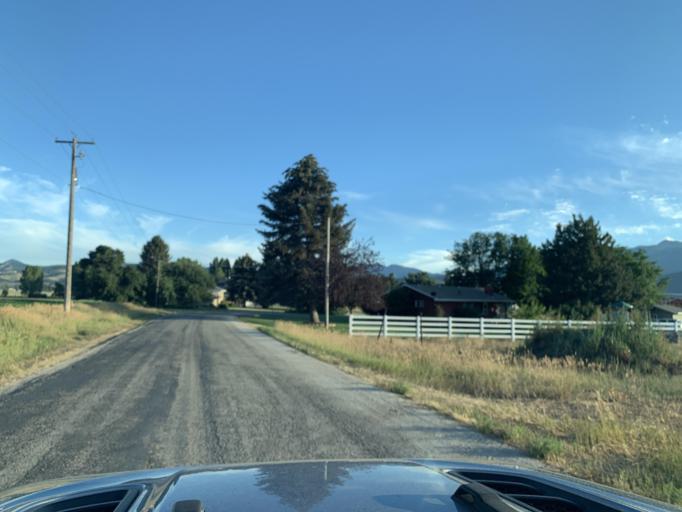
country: US
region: Utah
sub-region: Weber County
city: Wolf Creek
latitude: 41.2835
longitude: -111.7586
